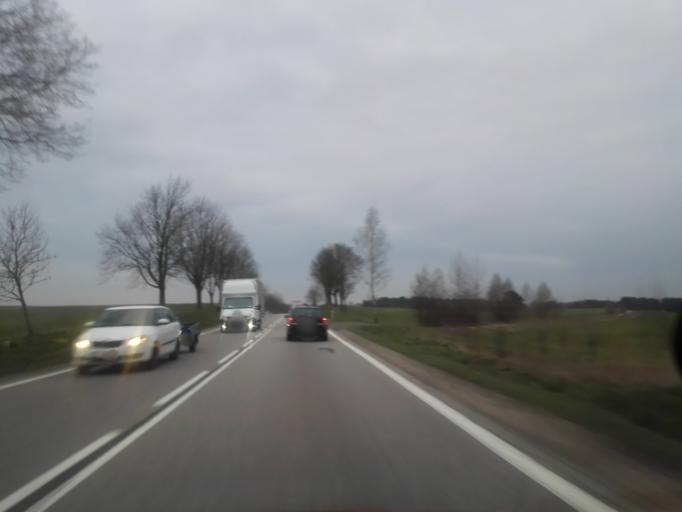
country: PL
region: Podlasie
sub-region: Powiat lomzynski
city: Piatnica
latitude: 53.2230
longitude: 22.1090
